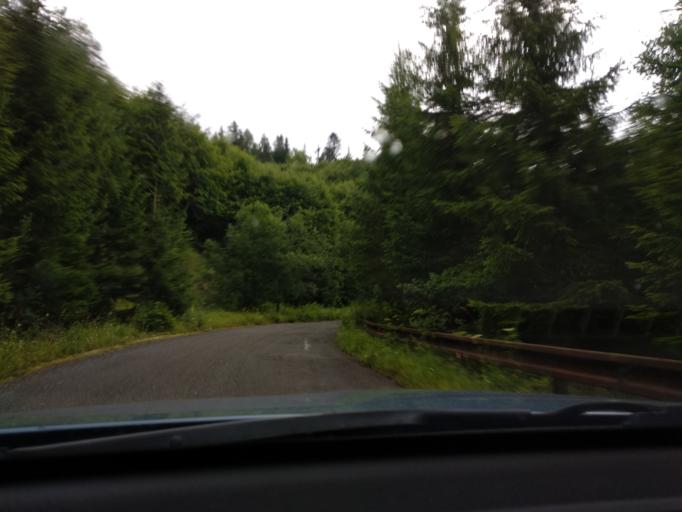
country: SK
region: Zilinsky
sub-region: Okres Liptovsky Mikulas
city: Hybe
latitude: 49.0260
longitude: 19.8885
